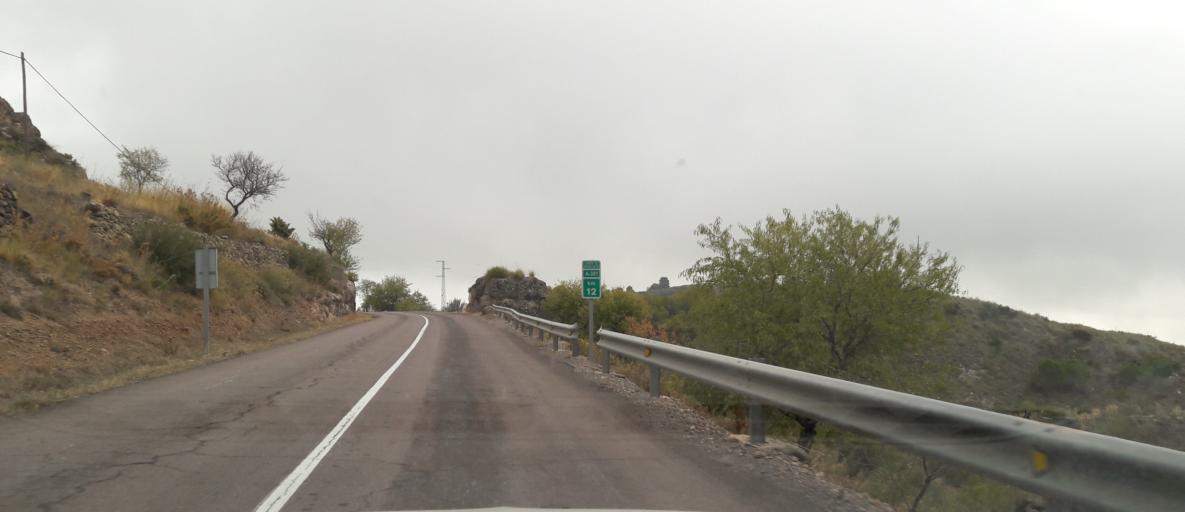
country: ES
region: Andalusia
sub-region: Provincia de Almeria
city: Enix
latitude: 36.8816
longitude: -2.6238
